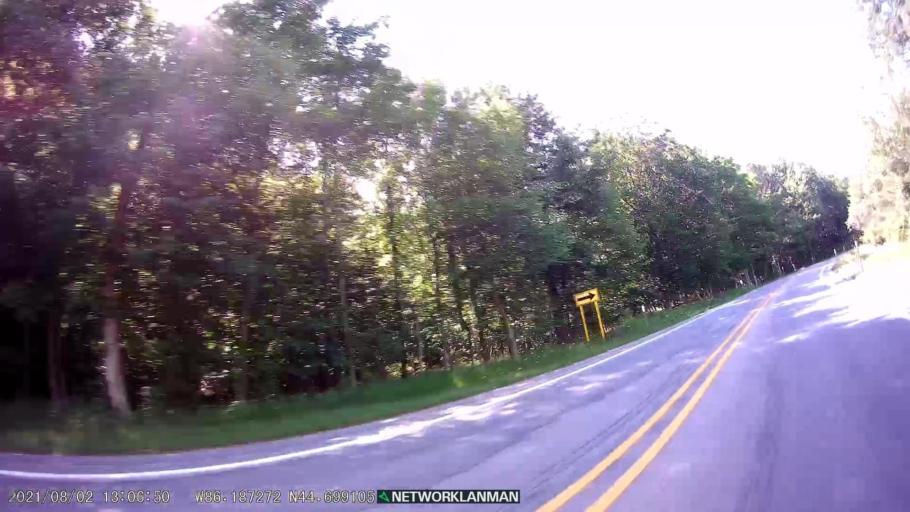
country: US
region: Michigan
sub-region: Benzie County
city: Frankfort
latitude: 44.6983
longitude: -86.1879
